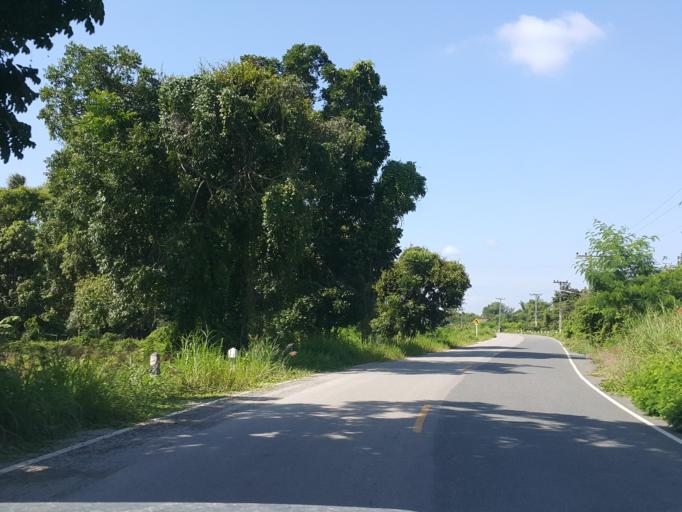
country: TH
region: Chiang Mai
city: Mae On
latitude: 18.7979
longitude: 99.1828
